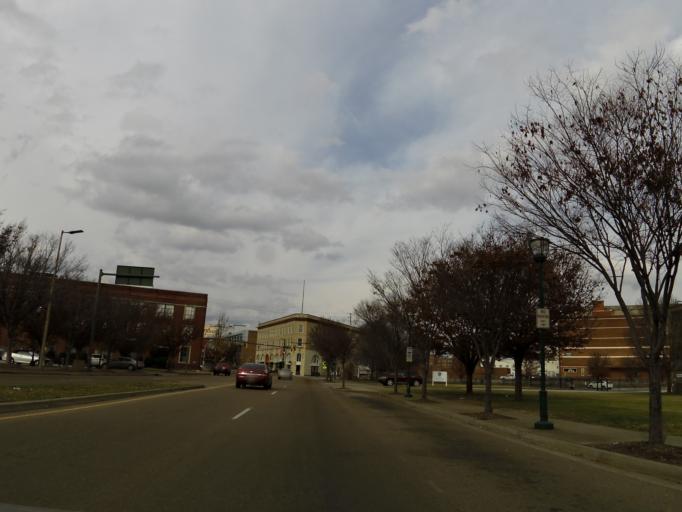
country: US
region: Tennessee
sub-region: Hamilton County
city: Chattanooga
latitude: 35.0386
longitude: -85.3074
